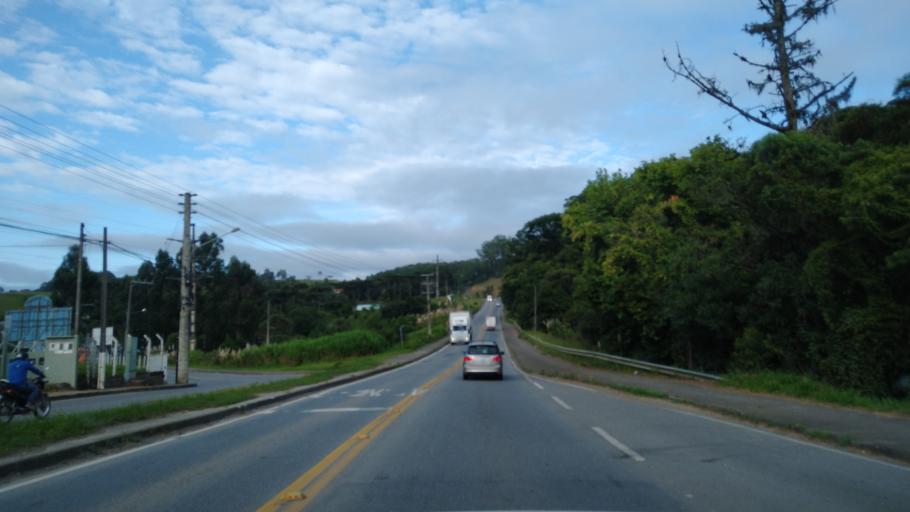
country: BR
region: Santa Catarina
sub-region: Sao Bento Do Sul
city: Sao Bento do Sul
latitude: -26.2276
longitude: -49.4194
